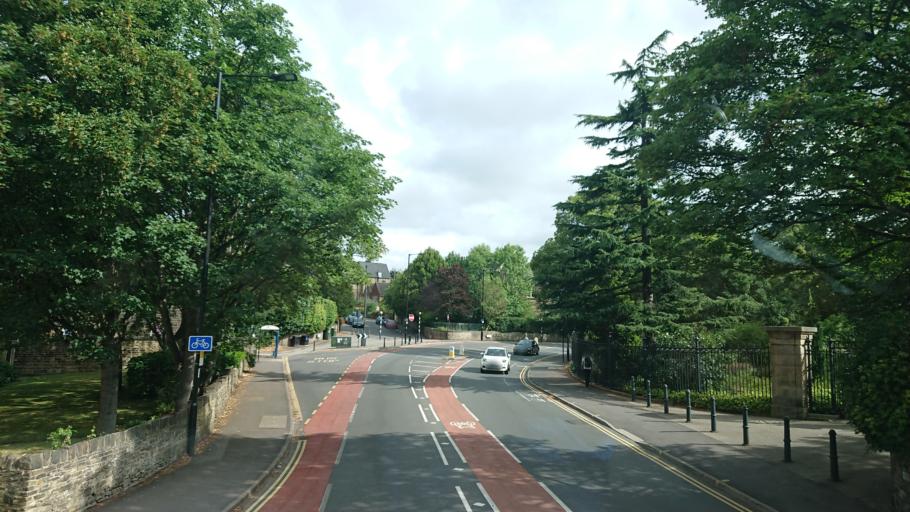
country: GB
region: England
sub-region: Sheffield
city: Sheffield
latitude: 53.3719
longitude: -1.5005
